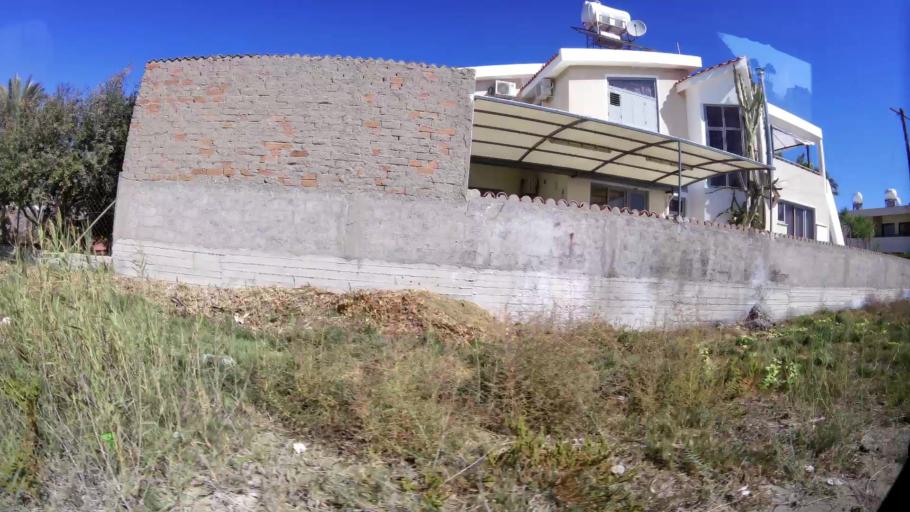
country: CY
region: Larnaka
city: Livadia
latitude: 34.9572
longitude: 33.6499
